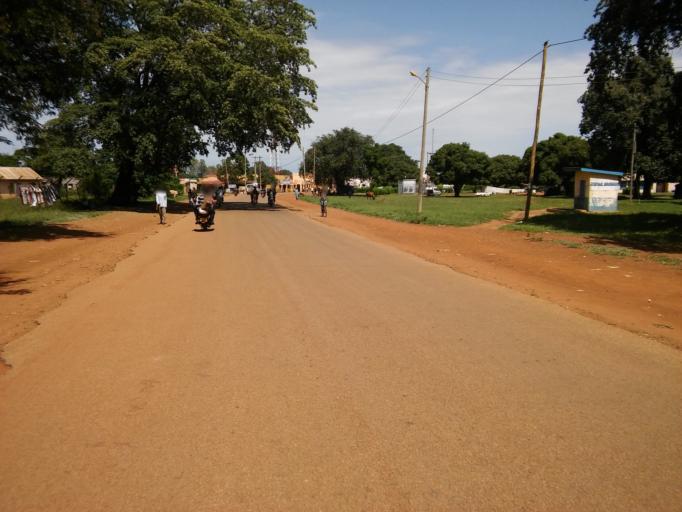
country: UG
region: Eastern Region
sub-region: Kumi District
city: Kumi
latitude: 1.4883
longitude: 33.9358
